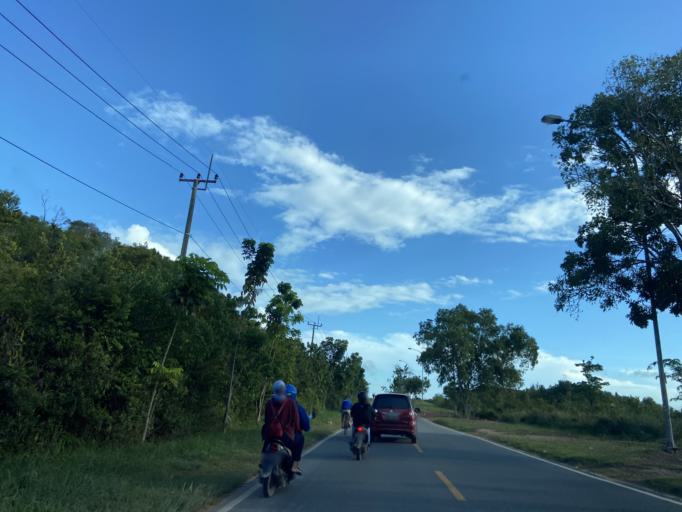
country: SG
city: Singapore
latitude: 0.9888
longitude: 104.0366
